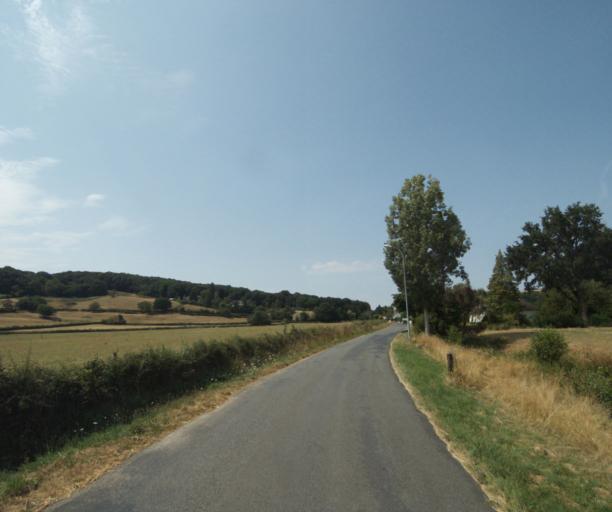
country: FR
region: Bourgogne
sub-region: Departement de Saone-et-Loire
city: Gueugnon
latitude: 46.6084
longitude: 4.0438
